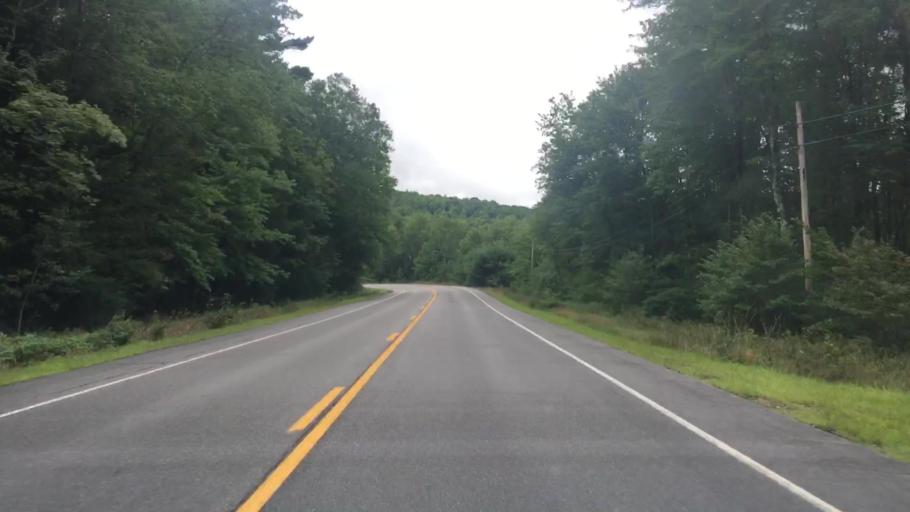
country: US
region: Maine
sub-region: York County
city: Cornish
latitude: 43.7808
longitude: -70.8243
